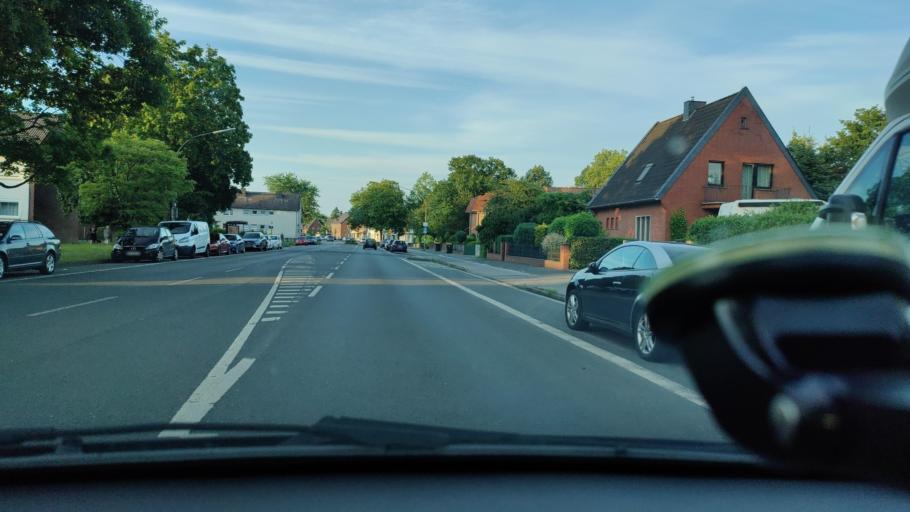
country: DE
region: North Rhine-Westphalia
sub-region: Regierungsbezirk Dusseldorf
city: Kamp-Lintfort
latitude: 51.4949
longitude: 6.5301
